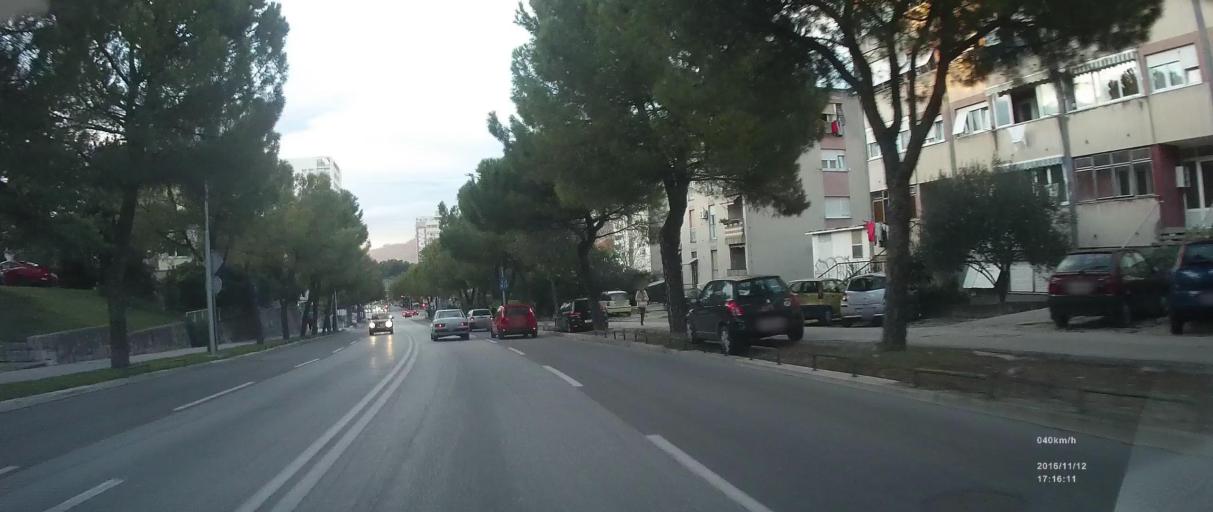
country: HR
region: Splitsko-Dalmatinska
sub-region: Grad Split
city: Split
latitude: 43.5155
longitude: 16.4485
